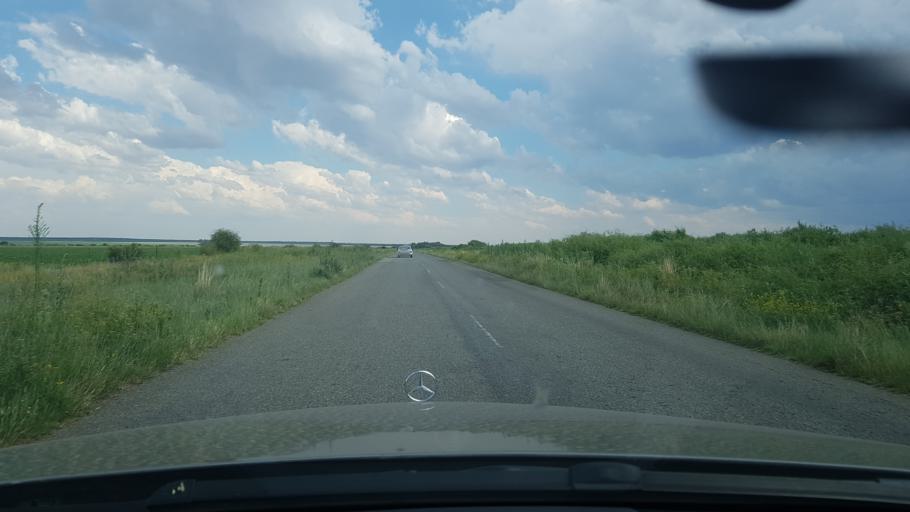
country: ZA
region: North-West
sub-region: Dr Ruth Segomotsi Mompati District Municipality
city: Bloemhof
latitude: -27.8369
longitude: 25.6398
